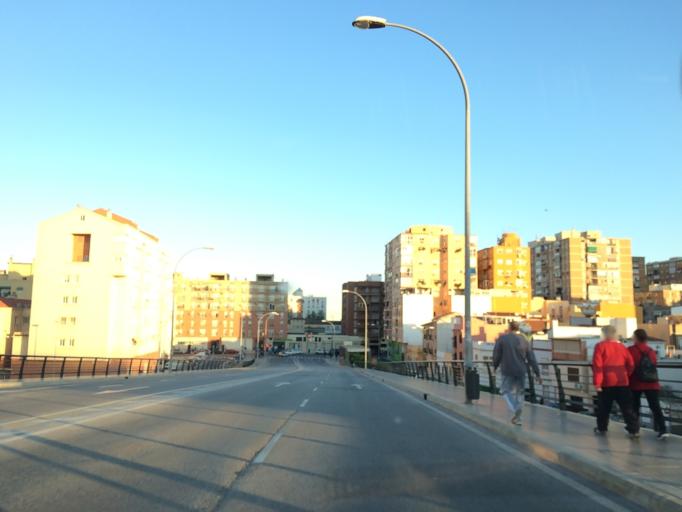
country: ES
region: Andalusia
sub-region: Provincia de Malaga
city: Malaga
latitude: 36.7092
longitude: -4.4367
